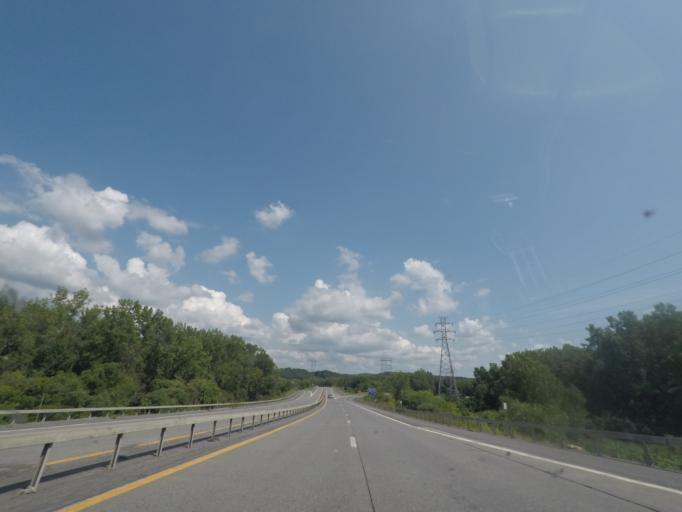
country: US
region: New York
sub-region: Albany County
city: Menands
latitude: 42.6842
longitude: -73.7268
